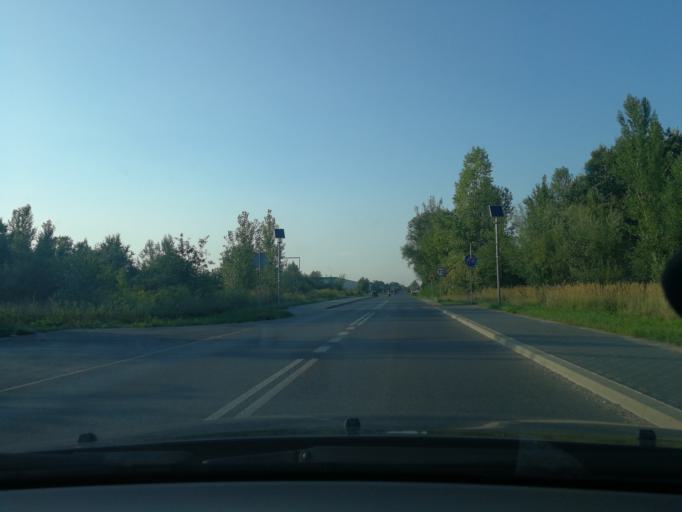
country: PL
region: Masovian Voivodeship
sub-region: Powiat pruszkowski
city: Brwinow
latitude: 52.1722
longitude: 20.7503
